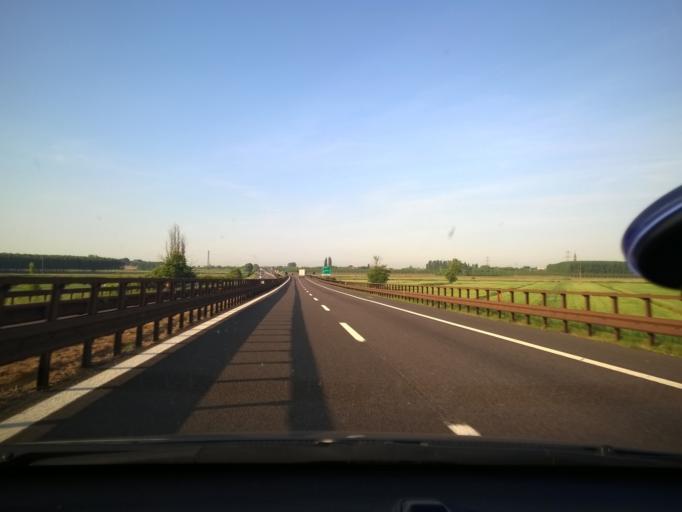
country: IT
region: Lombardy
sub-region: Provincia di Mantova
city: San Biagio
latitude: 45.1052
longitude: 10.8606
